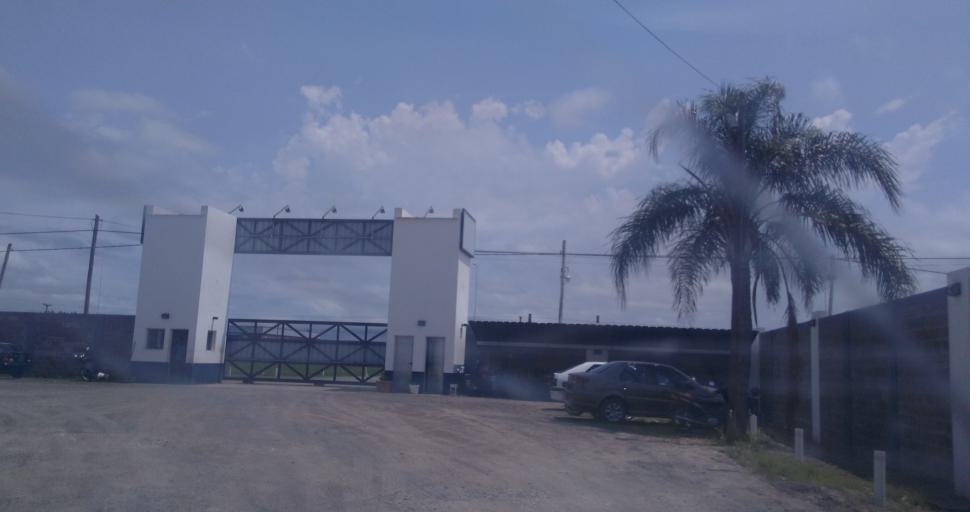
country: AR
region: Chaco
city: Fontana
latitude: -27.4617
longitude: -59.0395
